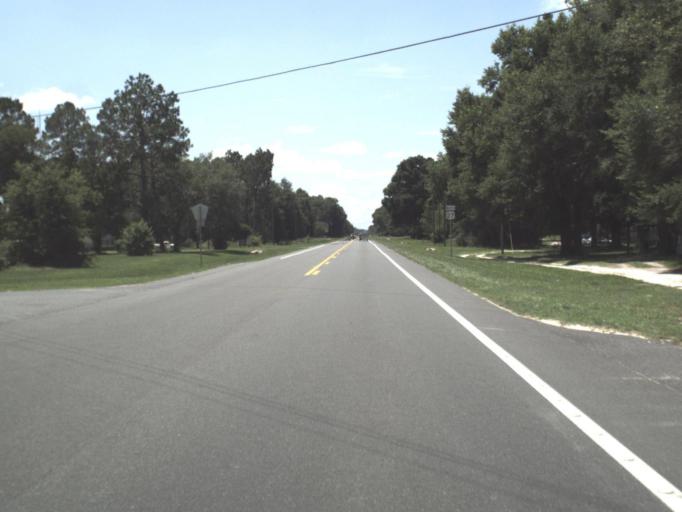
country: US
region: Florida
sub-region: Lafayette County
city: Mayo
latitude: 30.0642
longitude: -83.1936
